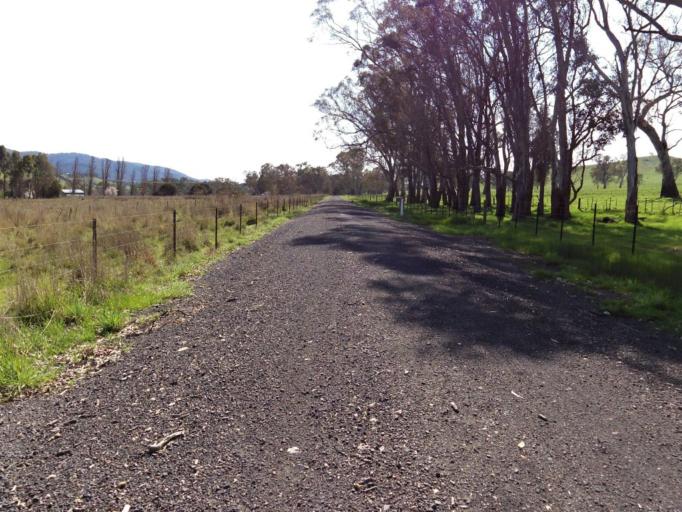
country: AU
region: Victoria
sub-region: Murrindindi
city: Alexandra
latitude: -37.1456
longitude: 145.5882
